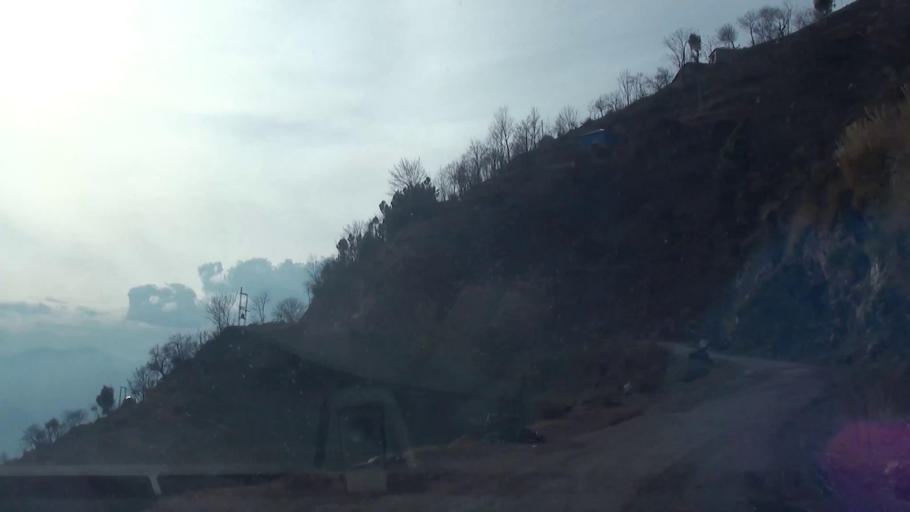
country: PK
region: Azad Kashmir
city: Muzaffarabad
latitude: 34.3690
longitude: 73.5225
